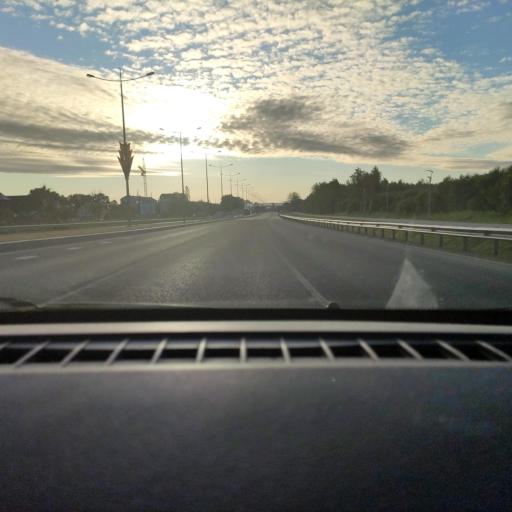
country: RU
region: Perm
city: Kondratovo
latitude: 57.9411
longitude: 56.0554
